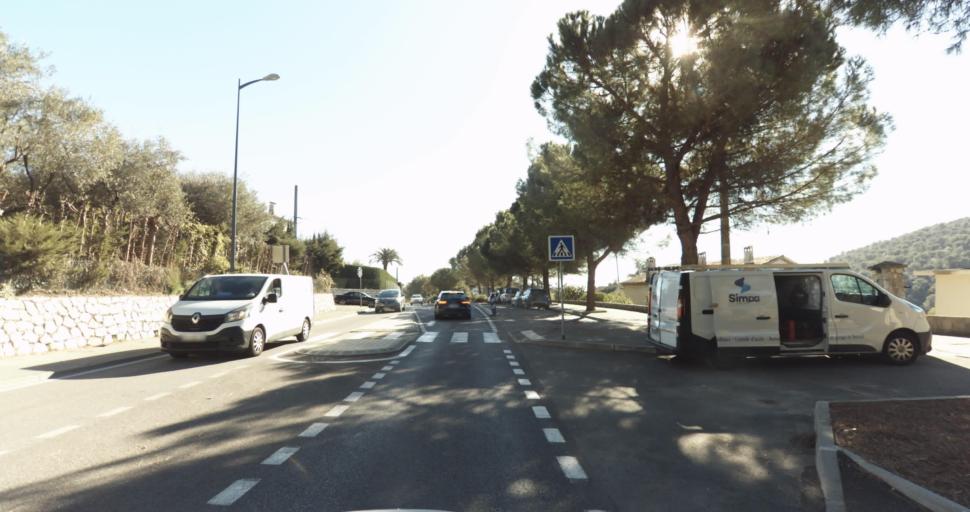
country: FR
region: Provence-Alpes-Cote d'Azur
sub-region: Departement des Alpes-Maritimes
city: Saint-Paul-de-Vence
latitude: 43.7118
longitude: 7.1250
